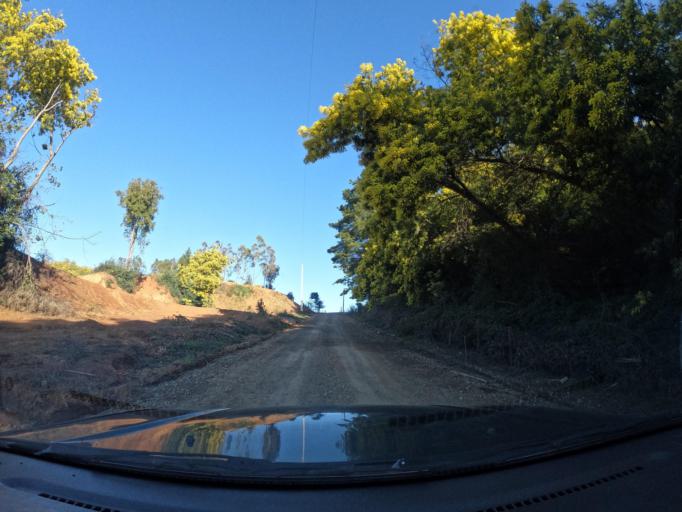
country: CL
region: Biobio
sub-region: Provincia de Concepcion
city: Chiguayante
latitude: -37.0169
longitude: -72.8582
